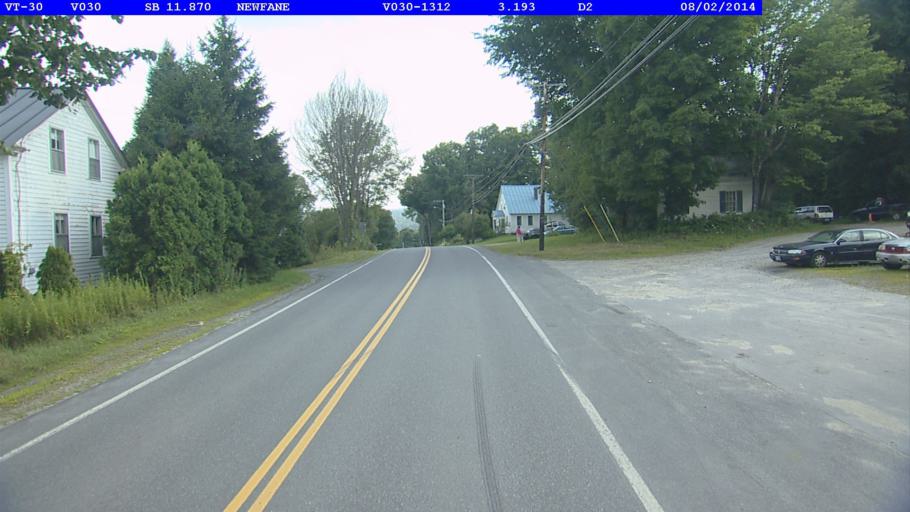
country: US
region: Vermont
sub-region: Windham County
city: Newfane
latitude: 42.9896
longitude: -72.6538
